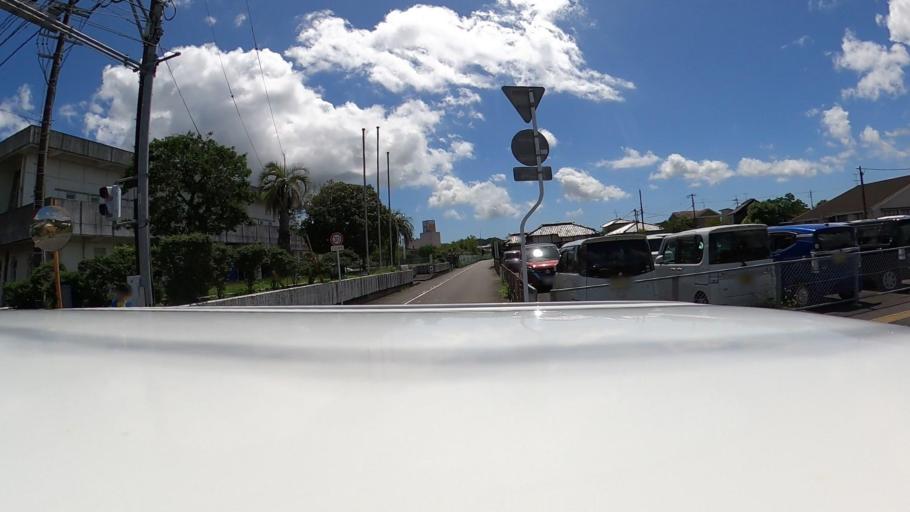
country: JP
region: Miyazaki
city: Tsuma
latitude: 32.1060
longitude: 131.4000
